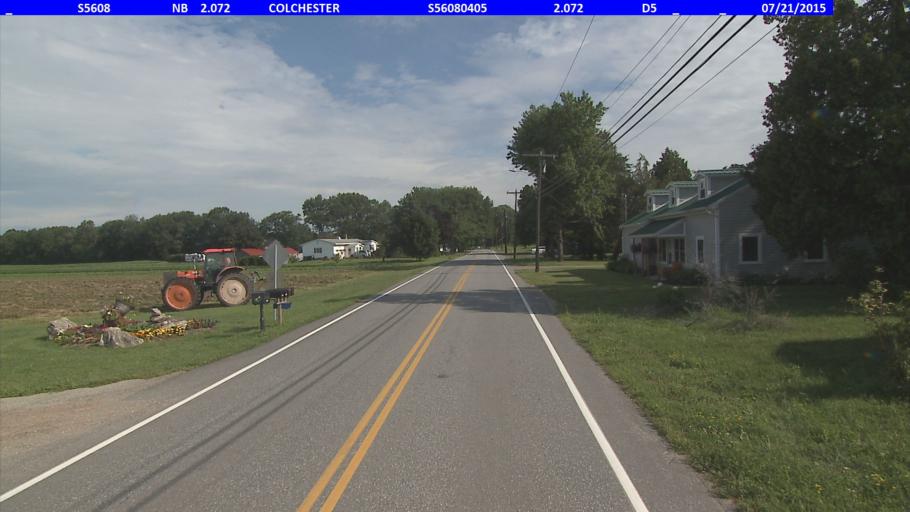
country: US
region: Vermont
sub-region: Chittenden County
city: Winooski
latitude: 44.5266
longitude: -73.2068
